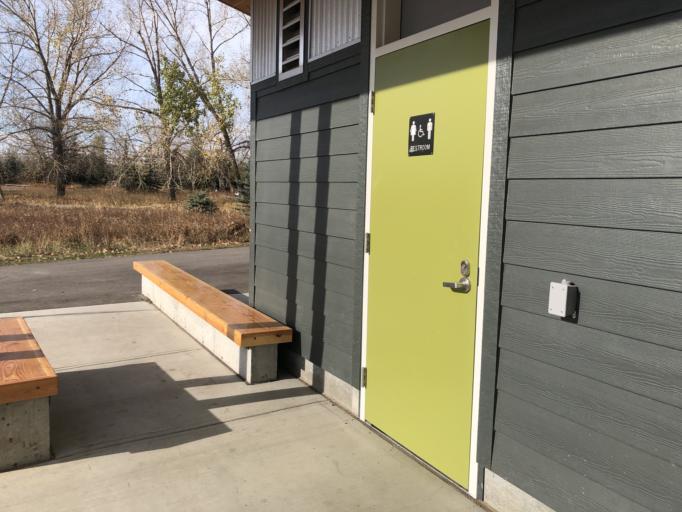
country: CA
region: Alberta
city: Calgary
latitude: 50.9268
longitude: -114.0672
